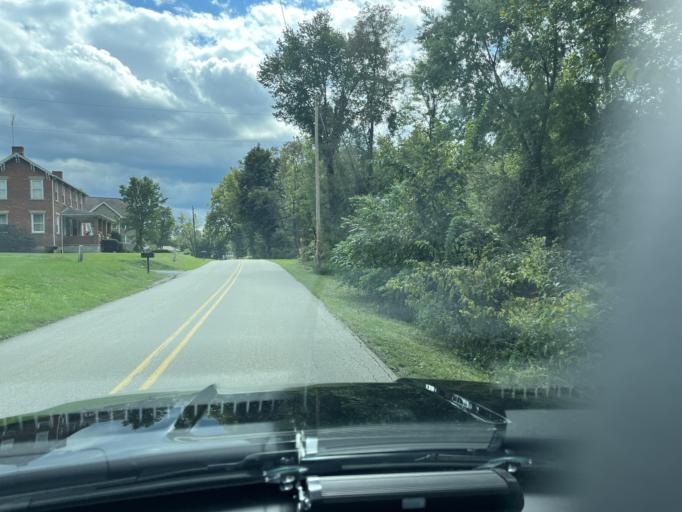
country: US
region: Pennsylvania
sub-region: Fayette County
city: Uniontown
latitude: 39.8850
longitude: -79.7150
